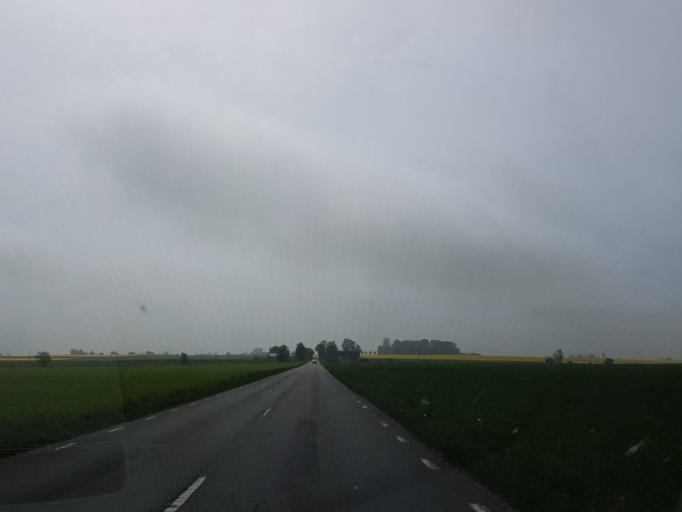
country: SE
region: Skane
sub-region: Tomelilla Kommun
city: Tomelilla
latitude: 55.4778
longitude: 14.0998
